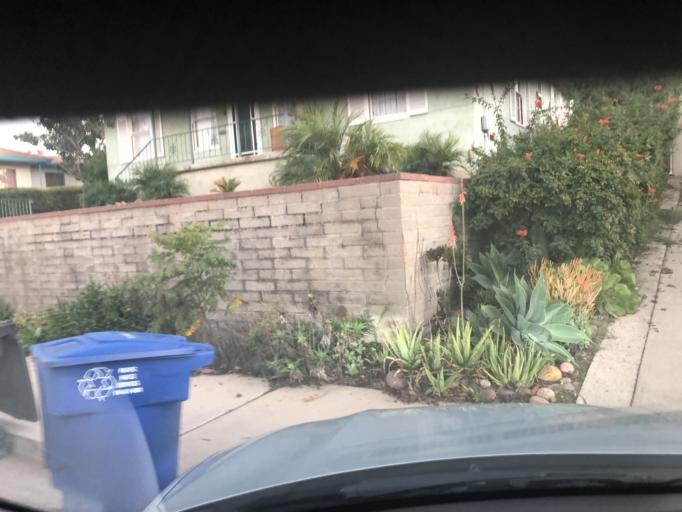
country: US
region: California
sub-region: San Diego County
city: Chula Vista
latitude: 32.6465
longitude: -117.0715
